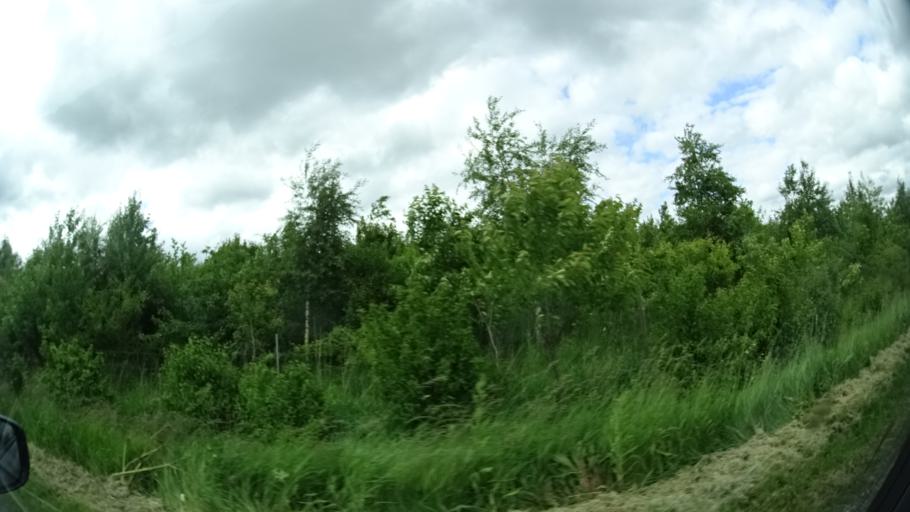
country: DK
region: Central Jutland
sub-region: Syddjurs Kommune
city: Ryomgard
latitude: 56.4058
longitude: 10.5452
